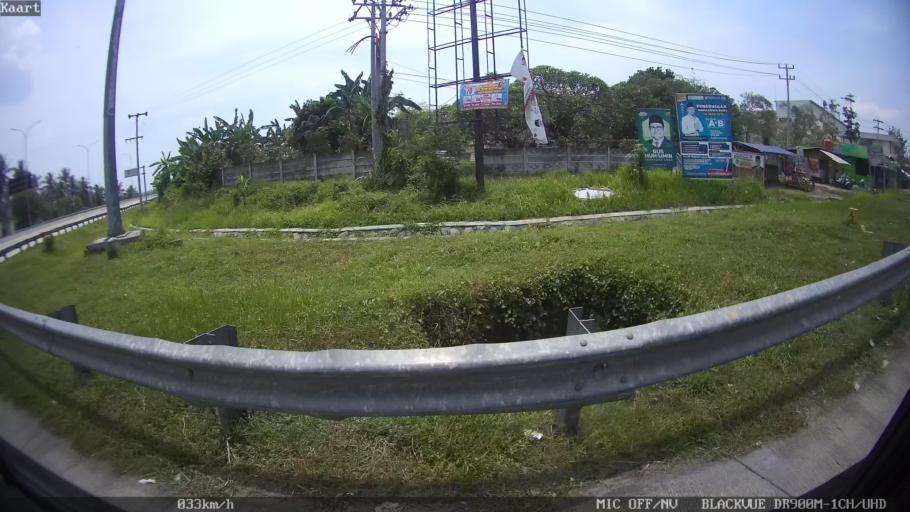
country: ID
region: Lampung
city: Natar
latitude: -5.2822
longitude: 105.1905
